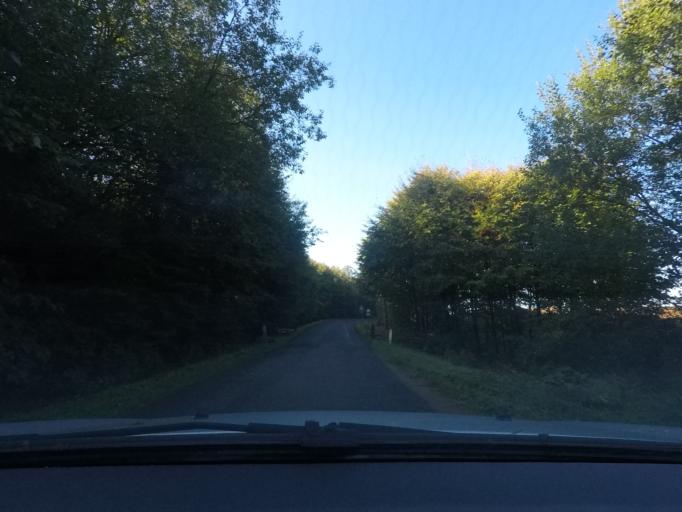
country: BE
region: Wallonia
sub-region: Province du Luxembourg
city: Musson
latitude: 49.6271
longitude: 5.7402
